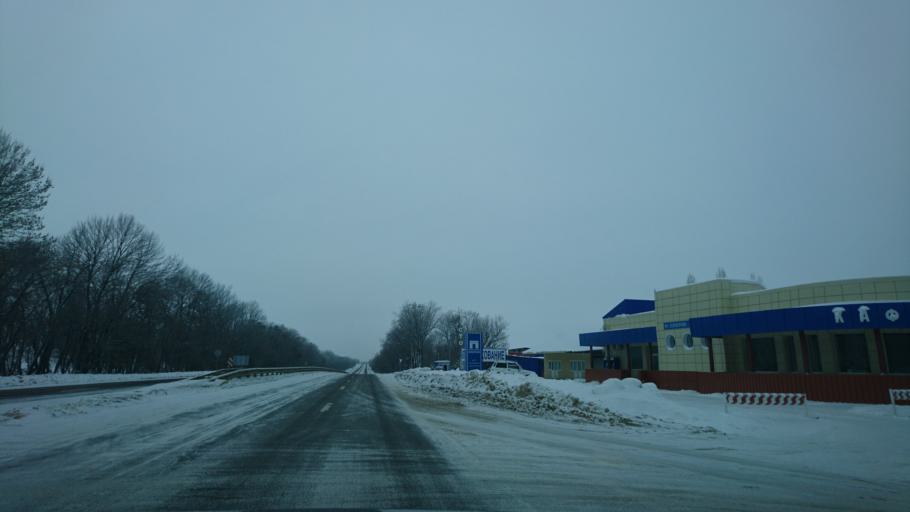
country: RU
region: Belgorod
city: Mayskiy
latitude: 50.4346
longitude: 36.3888
